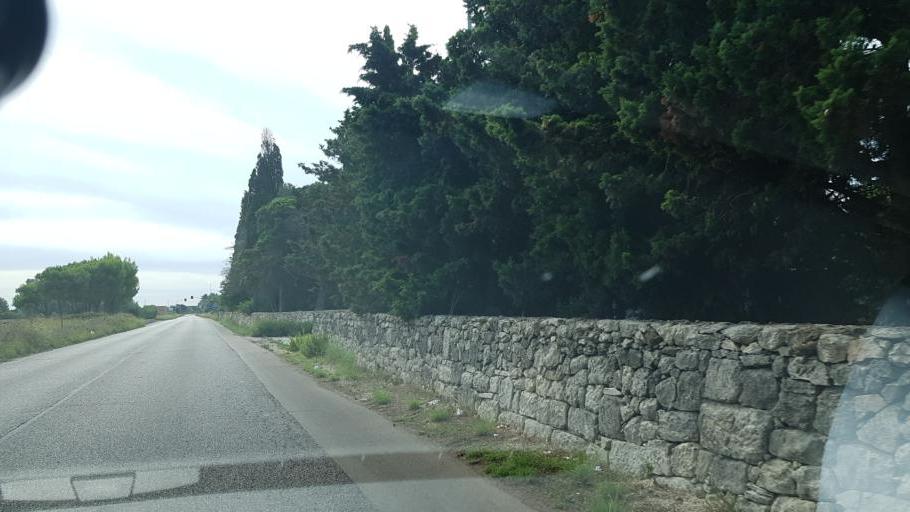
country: IT
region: Apulia
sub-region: Provincia di Lecce
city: Borgagne
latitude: 40.2607
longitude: 18.4346
